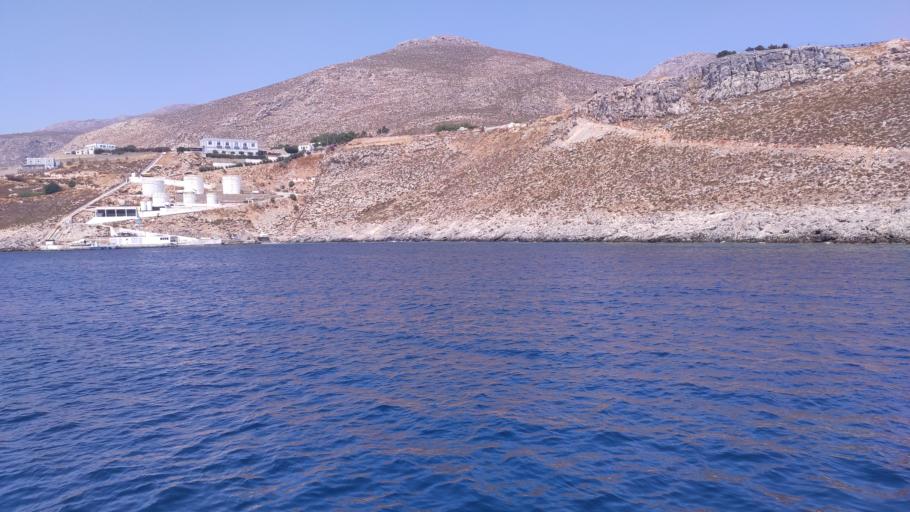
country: GR
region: South Aegean
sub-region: Nomos Dodekanisou
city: Kalymnos
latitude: 36.9467
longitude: 27.0082
